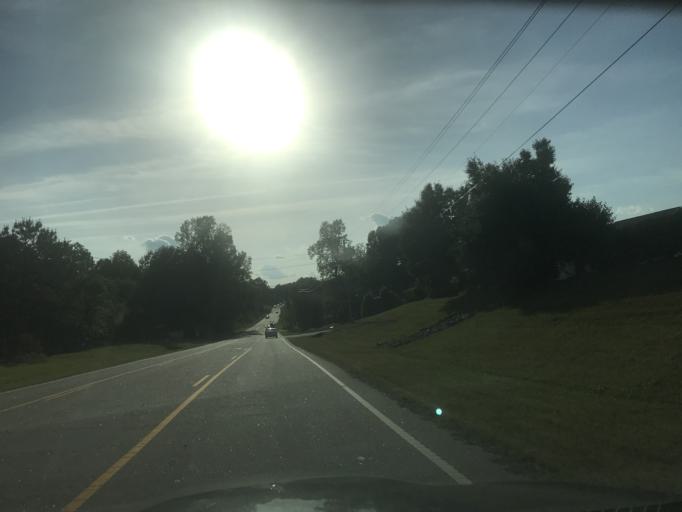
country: US
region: North Carolina
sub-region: Wake County
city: Knightdale
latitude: 35.7483
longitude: -78.4617
